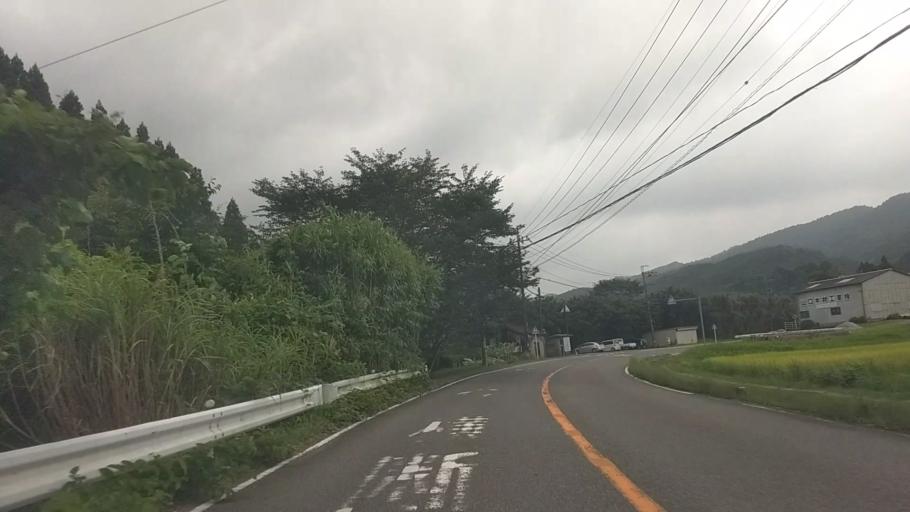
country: JP
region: Chiba
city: Kawaguchi
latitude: 35.1382
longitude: 139.9783
